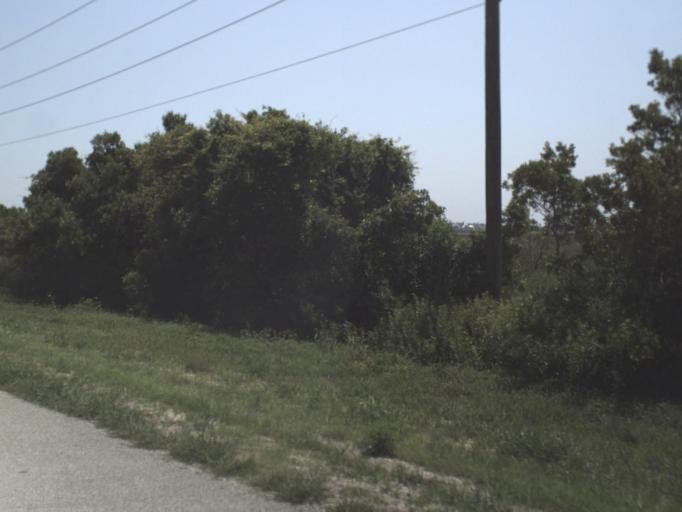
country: US
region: Florida
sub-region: Saint Johns County
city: Butler Beach
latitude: 29.7613
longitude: -81.2665
